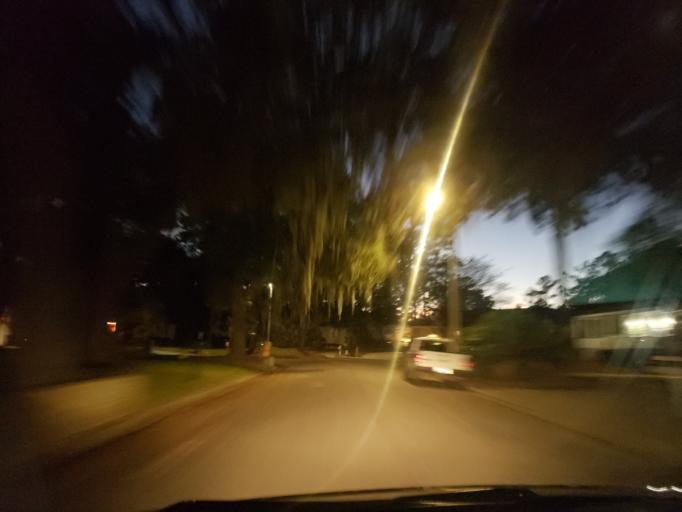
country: US
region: Georgia
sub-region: Chatham County
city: Isle of Hope
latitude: 31.9858
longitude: -81.0655
